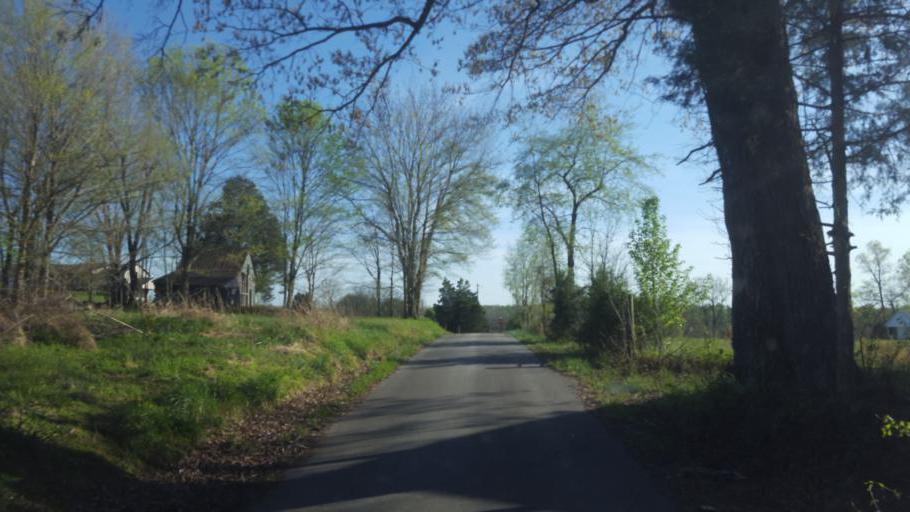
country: US
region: Kentucky
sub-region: Barren County
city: Cave City
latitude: 37.1758
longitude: -85.9976
